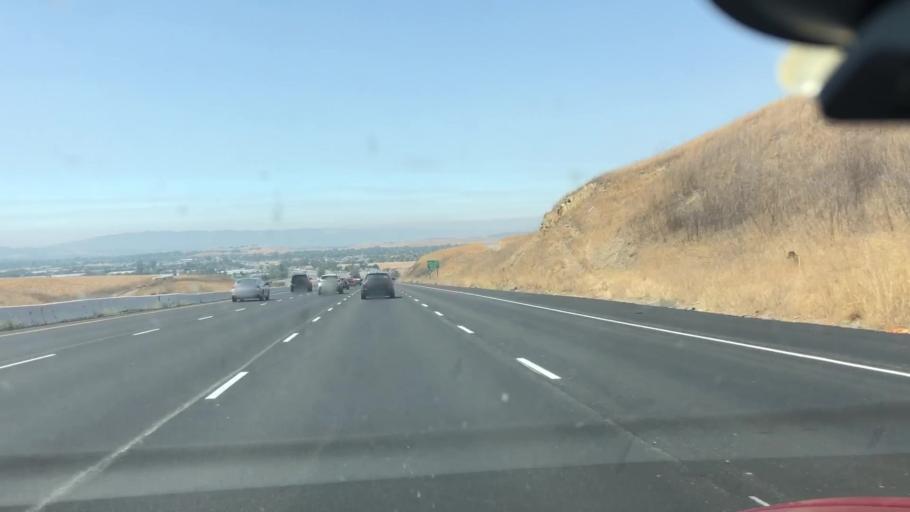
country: US
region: California
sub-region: Alameda County
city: Livermore
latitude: 37.7197
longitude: -121.6874
